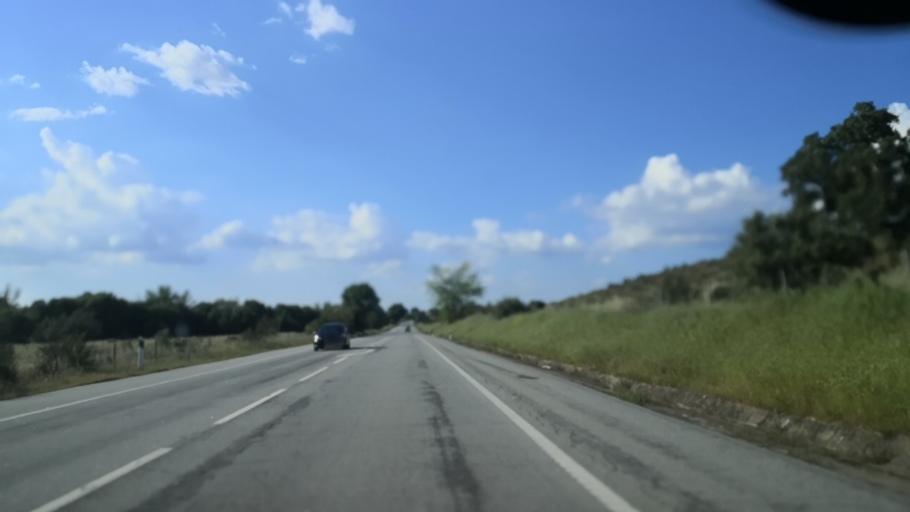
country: PT
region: Portalegre
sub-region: Portalegre
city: Urra
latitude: 39.0788
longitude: -7.4364
